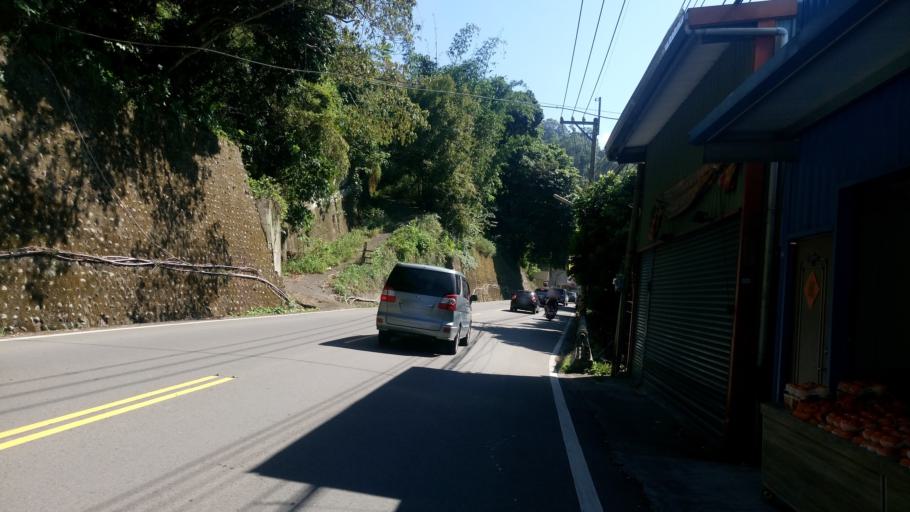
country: TW
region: Taiwan
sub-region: Hsinchu
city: Zhubei
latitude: 24.7107
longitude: 121.1720
